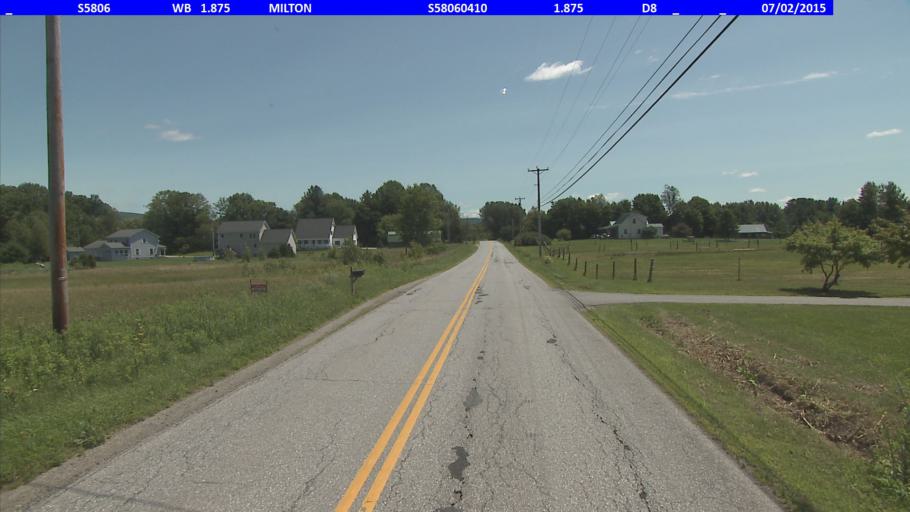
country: US
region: Vermont
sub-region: Chittenden County
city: Milton
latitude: 44.6608
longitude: -73.1474
